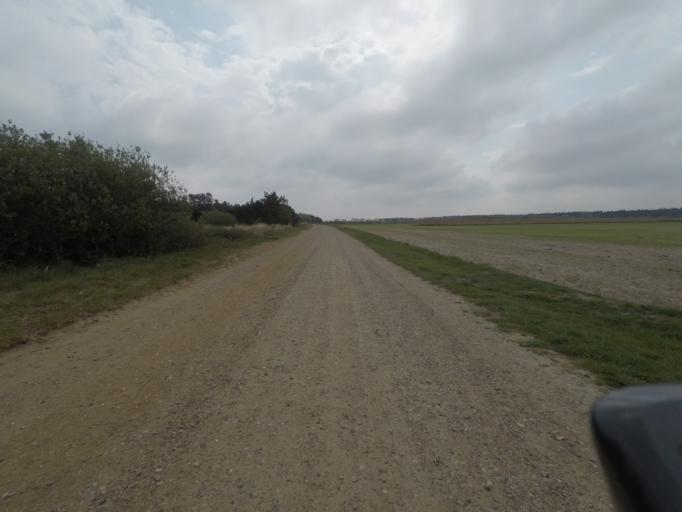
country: DE
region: Schleswig-Holstein
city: List
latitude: 55.0899
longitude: 8.5223
